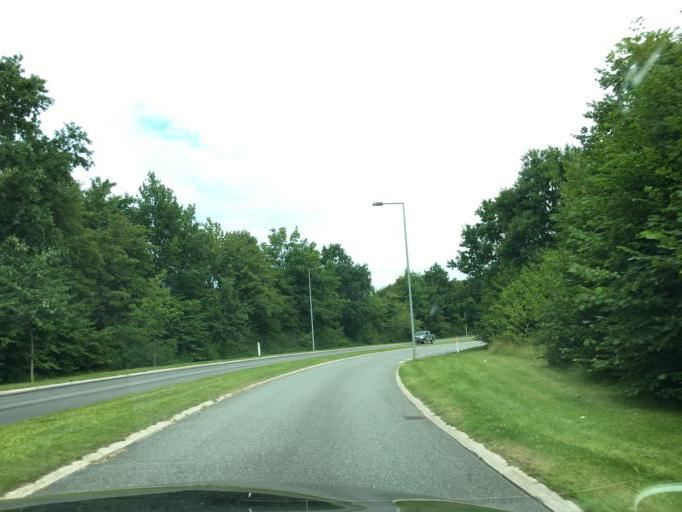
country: DK
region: Capital Region
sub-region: Horsholm Kommune
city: Horsholm
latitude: 55.8810
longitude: 12.4939
